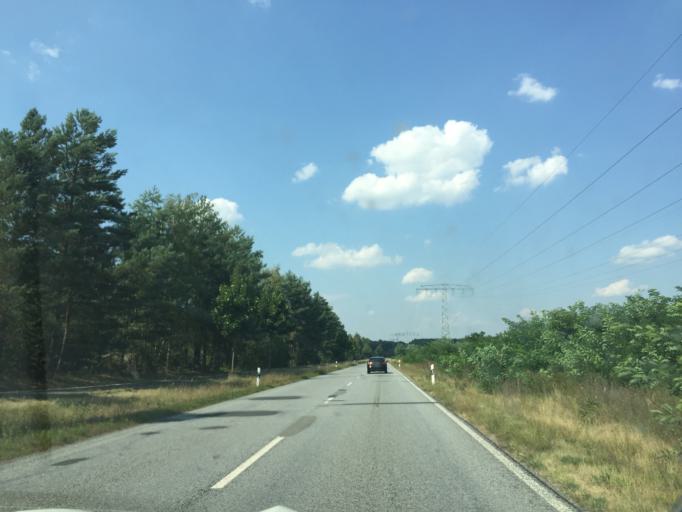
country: DE
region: Saxony
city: Boxberg
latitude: 51.4272
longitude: 14.5368
